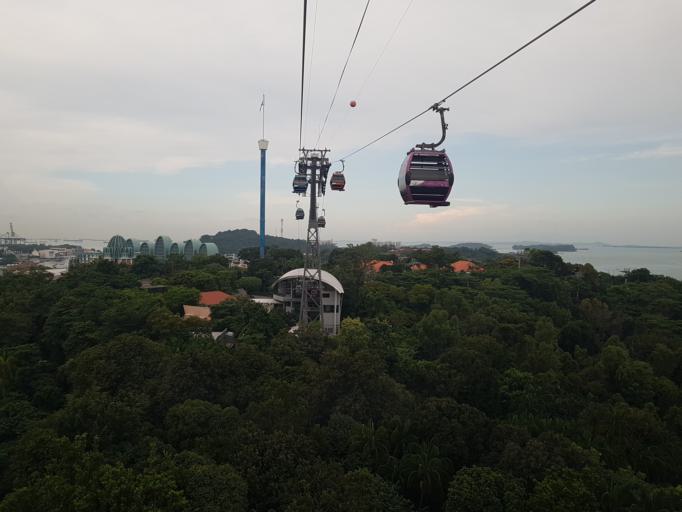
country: SG
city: Singapore
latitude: 1.2558
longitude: 103.8150
